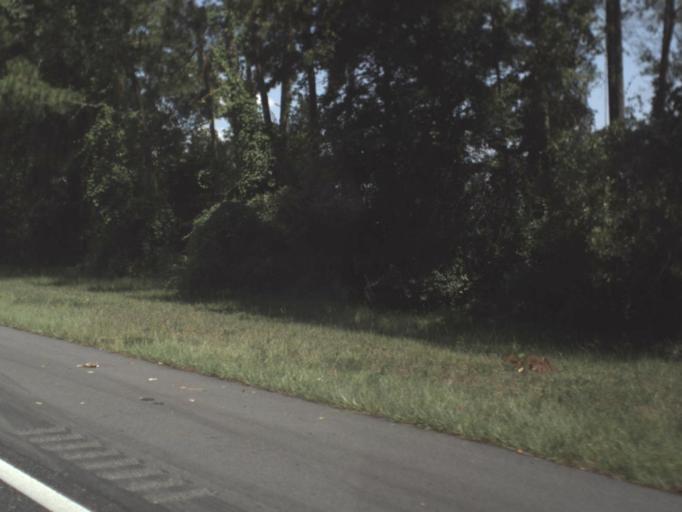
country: US
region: Florida
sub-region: Madison County
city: Madison
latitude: 30.3634
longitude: -83.2237
